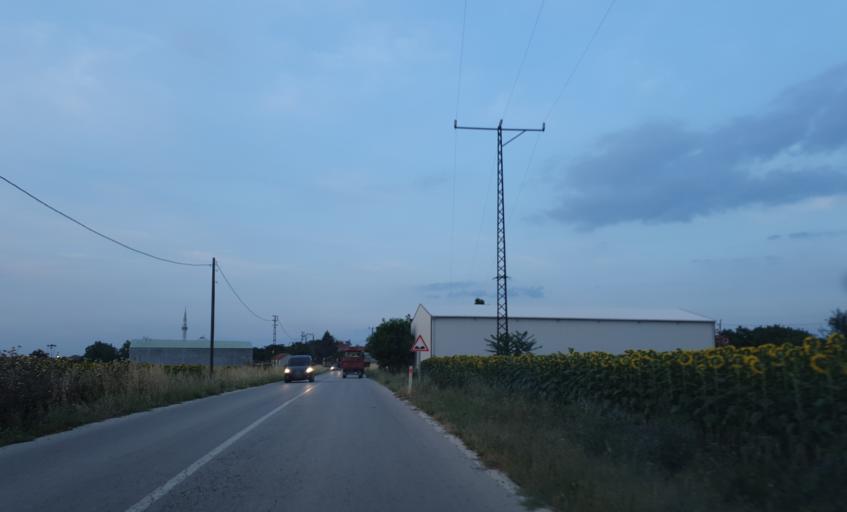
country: TR
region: Tekirdag
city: Beyazkoy
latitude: 41.4092
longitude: 27.6511
